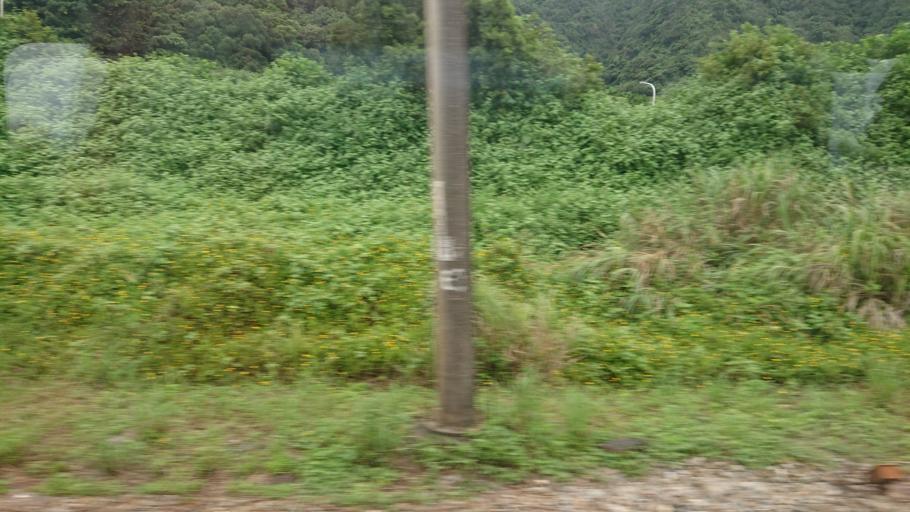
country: TW
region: Taiwan
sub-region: Keelung
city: Keelung
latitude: 24.9628
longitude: 121.9204
